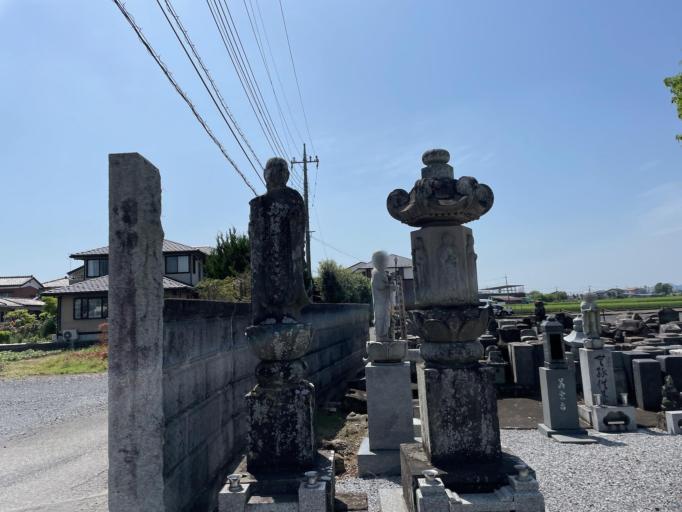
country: JP
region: Tochigi
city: Ashikaga
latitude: 36.3035
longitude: 139.4876
